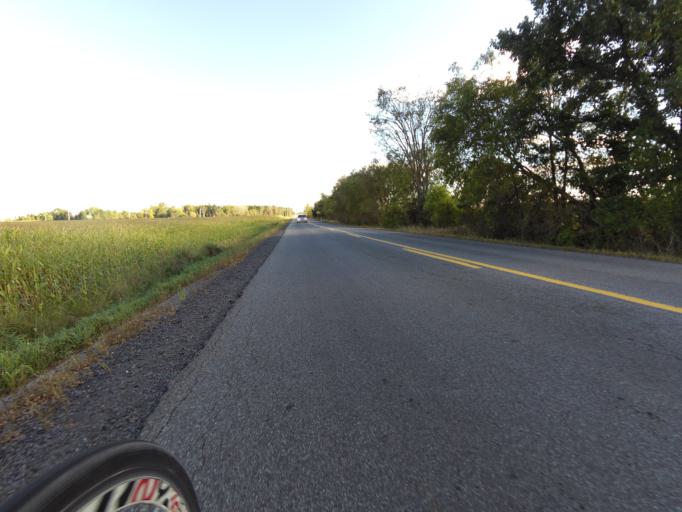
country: CA
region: Ontario
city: Bells Corners
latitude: 45.1244
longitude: -75.7417
